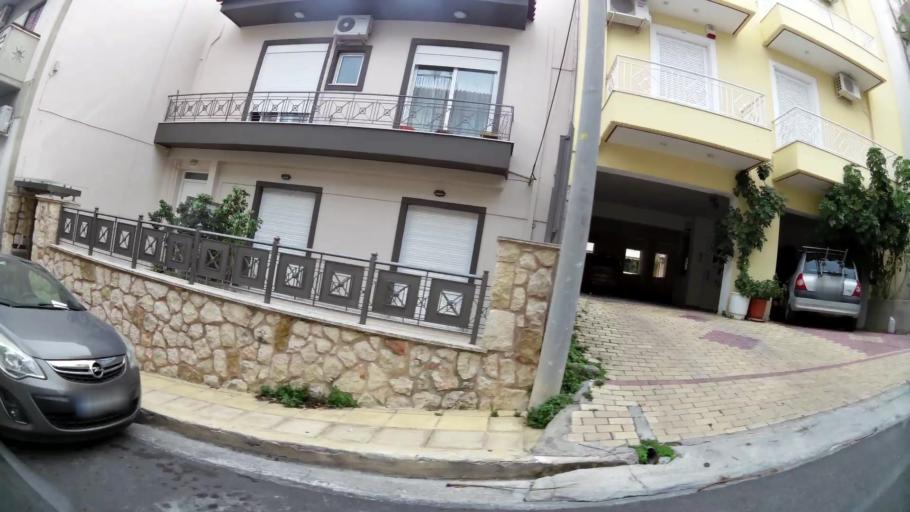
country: GR
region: Attica
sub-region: Nomarchia Athinas
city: Agios Dimitrios
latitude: 37.9301
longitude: 23.7415
